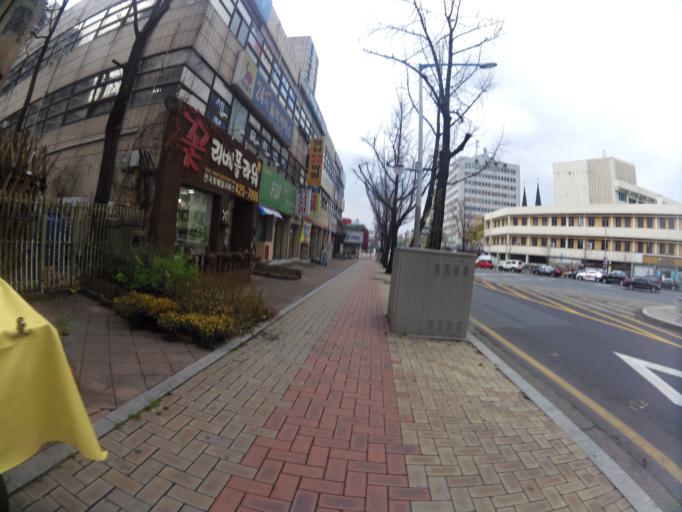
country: KR
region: Daegu
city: Daegu
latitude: 35.8670
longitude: 128.5868
